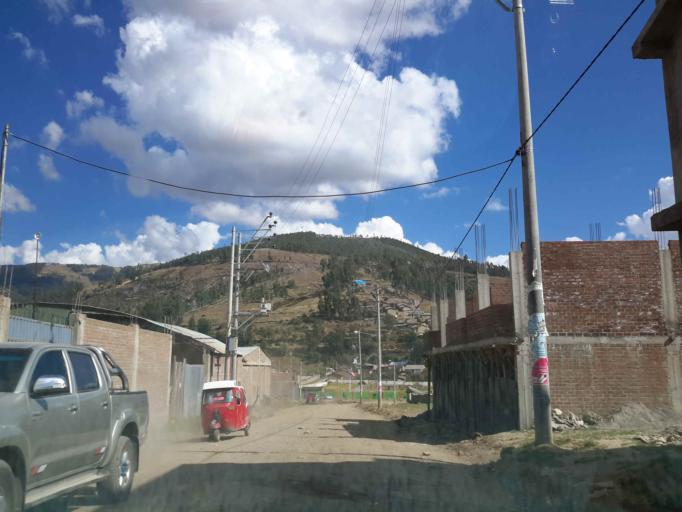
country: PE
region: Apurimac
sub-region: Provincia de Andahuaylas
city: Talavera
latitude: -13.6558
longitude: -73.4316
